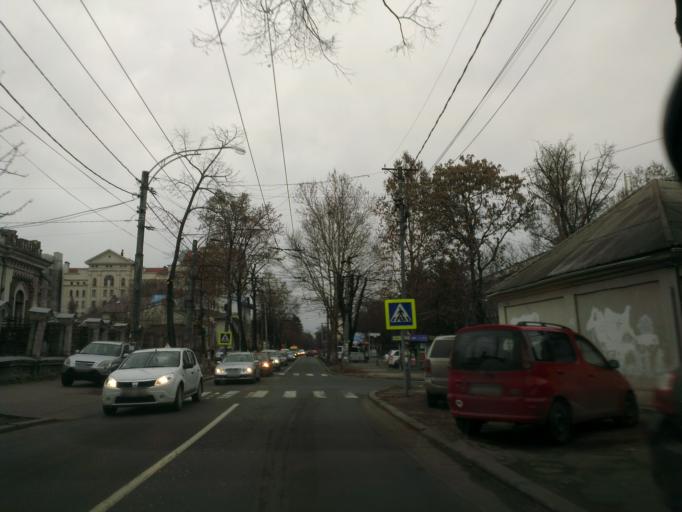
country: MD
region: Chisinau
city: Chisinau
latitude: 47.0169
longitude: 28.8248
